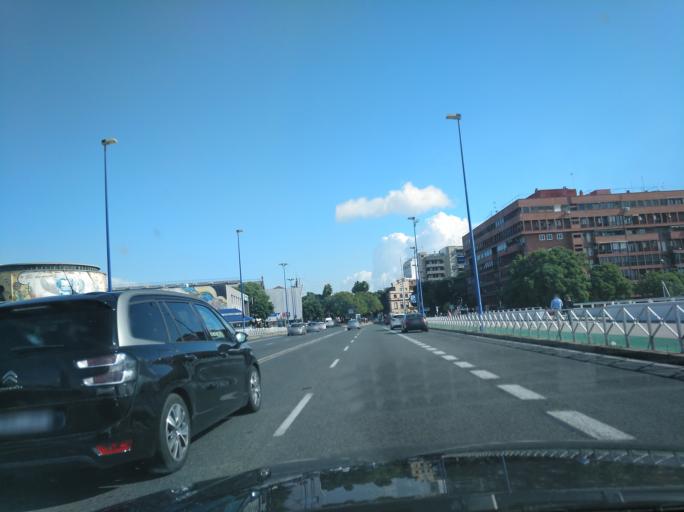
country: ES
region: Andalusia
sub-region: Provincia de Sevilla
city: Camas
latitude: 37.3905
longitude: -6.0051
